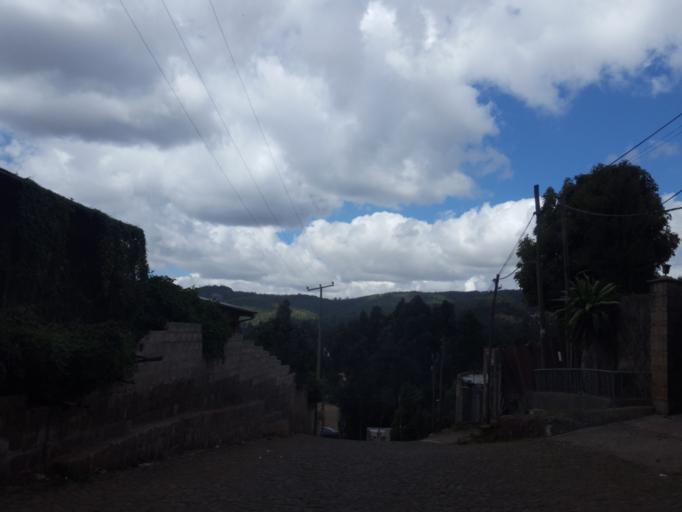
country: ET
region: Adis Abeba
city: Addis Ababa
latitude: 9.0648
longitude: 38.7317
